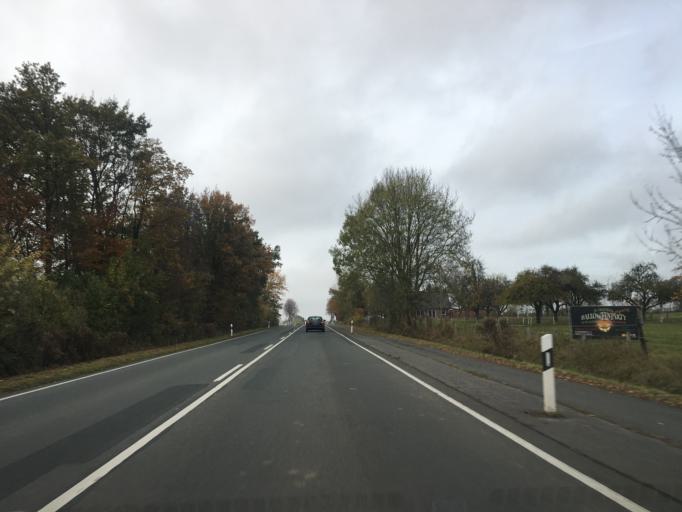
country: DE
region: North Rhine-Westphalia
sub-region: Regierungsbezirk Munster
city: Altenberge
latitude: 52.0308
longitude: 7.4848
